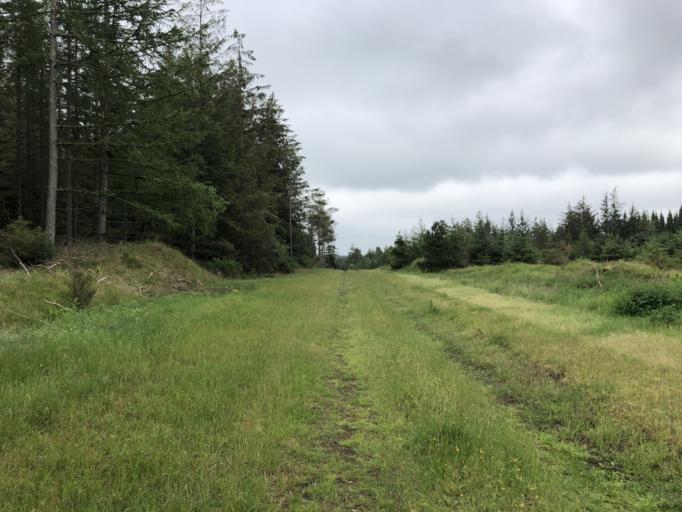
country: DK
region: Central Jutland
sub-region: Holstebro Kommune
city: Ulfborg
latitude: 56.2517
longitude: 8.3594
